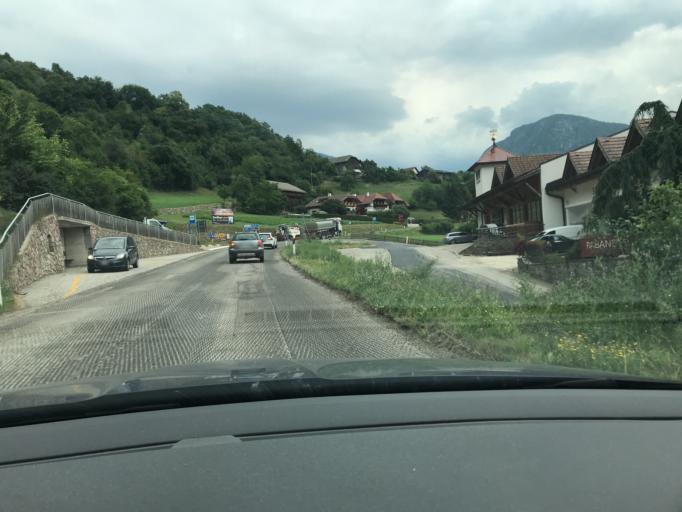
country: IT
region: Trentino-Alto Adige
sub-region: Bolzano
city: Laion
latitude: 46.6020
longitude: 11.5598
